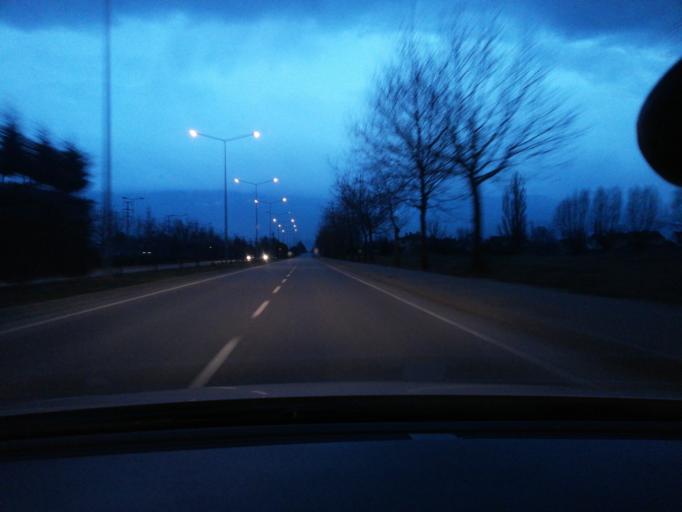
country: TR
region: Bolu
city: Bolu
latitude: 40.7165
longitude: 31.6145
